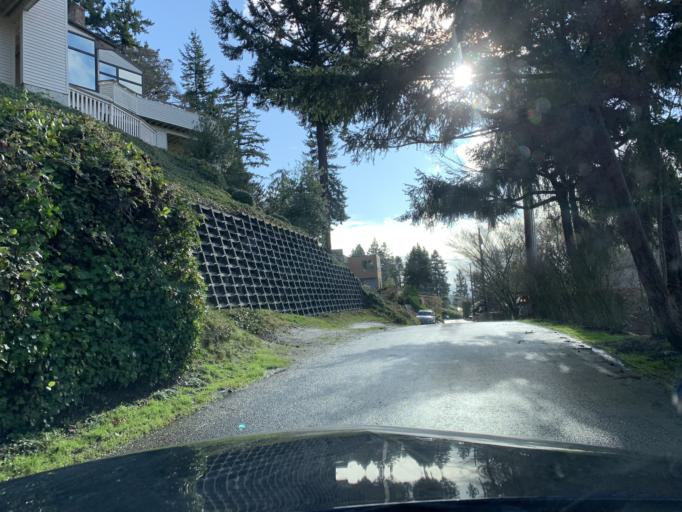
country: US
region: Washington
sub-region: King County
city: Mercer Island
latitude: 47.5841
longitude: -122.2470
